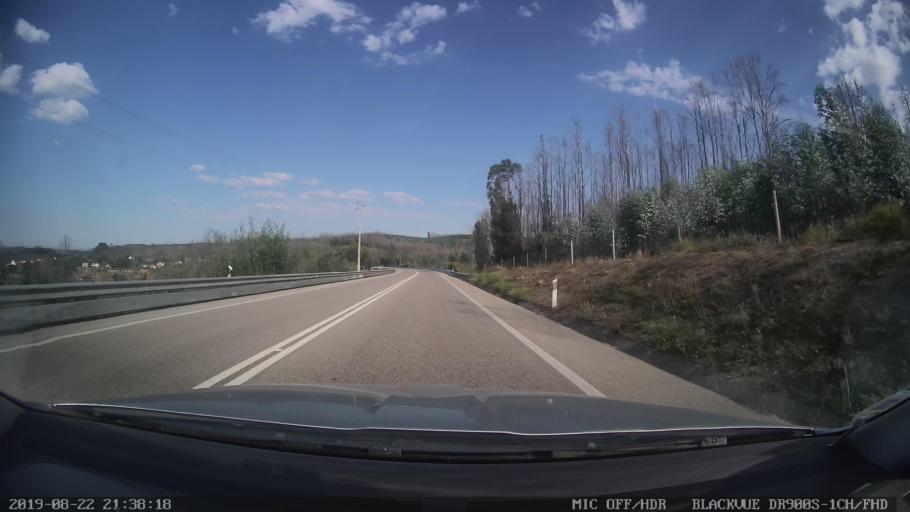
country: PT
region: Leiria
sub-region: Figueiro Dos Vinhos
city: Figueiro dos Vinhos
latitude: 39.9352
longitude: -8.2654
